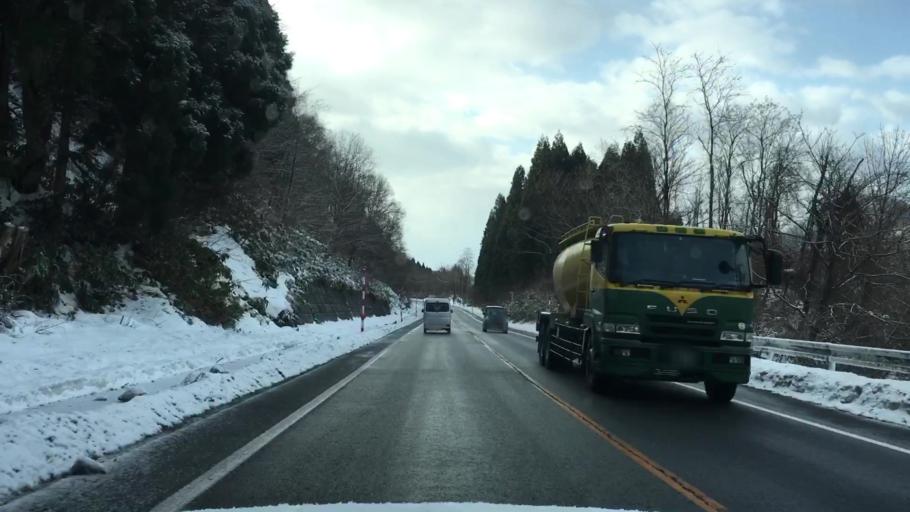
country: JP
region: Akita
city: Odate
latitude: 40.3942
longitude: 140.6054
